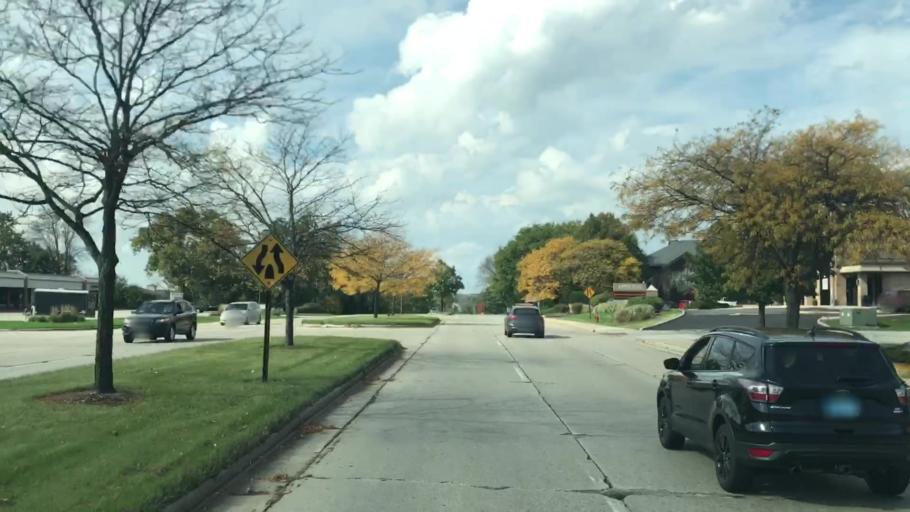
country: US
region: Wisconsin
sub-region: Waukesha County
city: Elm Grove
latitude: 43.0600
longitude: -88.0687
